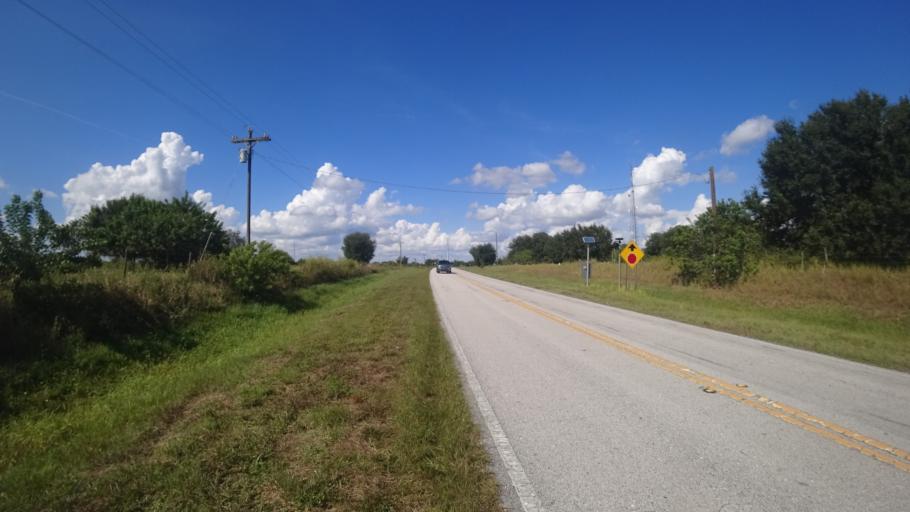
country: US
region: Florida
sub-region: Sarasota County
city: The Meadows
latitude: 27.4715
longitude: -82.3056
